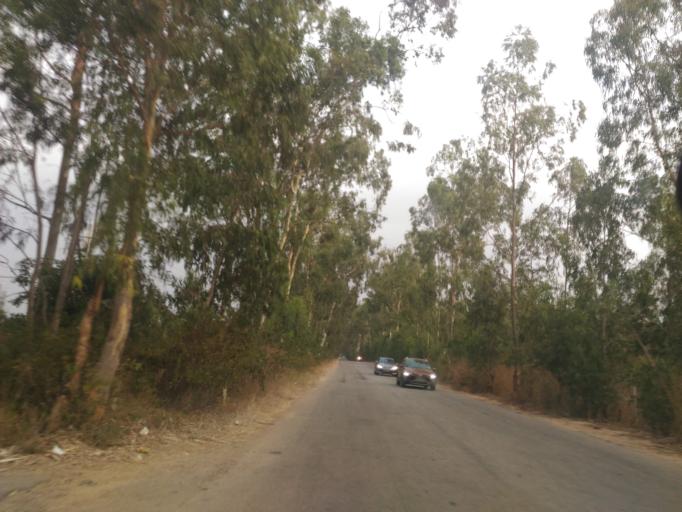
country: IN
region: Karnataka
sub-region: Chikkaballapur
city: Chik Ballapur
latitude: 13.3470
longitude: 77.6769
